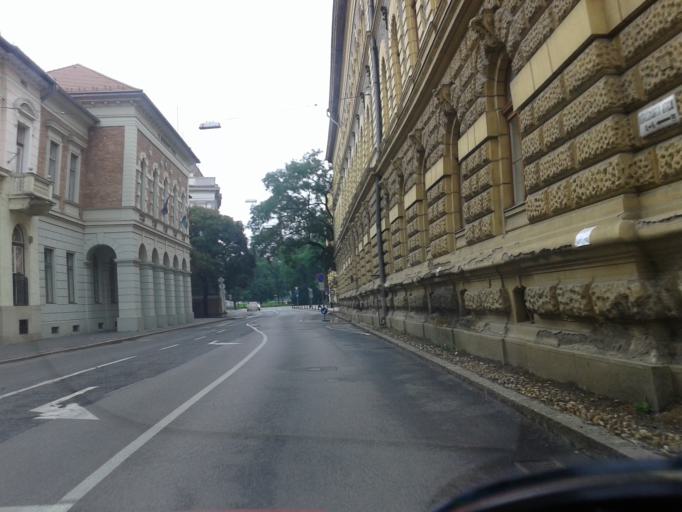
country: HU
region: Csongrad
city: Szeged
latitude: 46.2543
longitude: 20.1508
